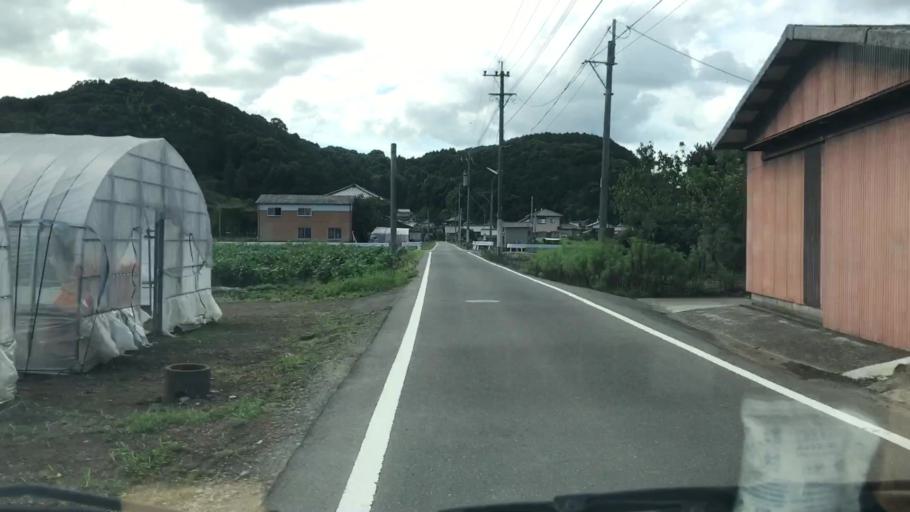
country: JP
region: Saga Prefecture
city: Kashima
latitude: 33.1168
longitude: 130.0735
